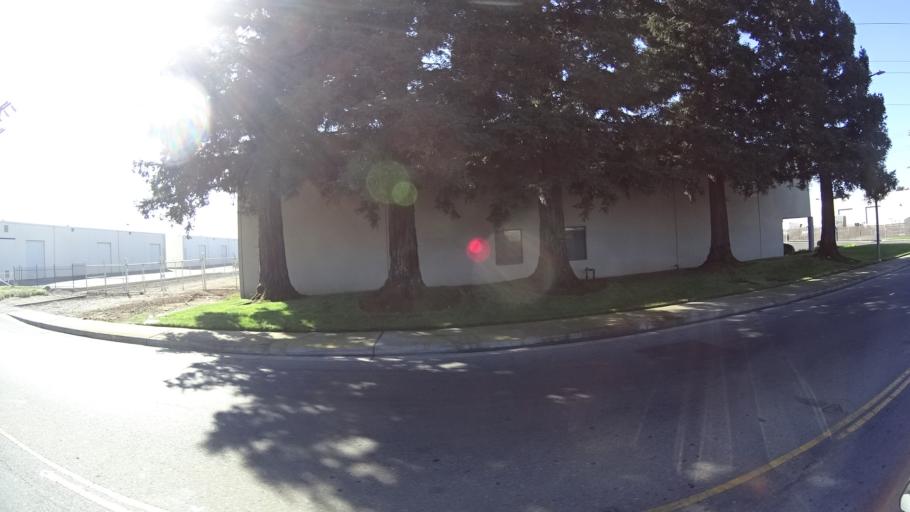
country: US
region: California
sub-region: Sacramento County
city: Rosemont
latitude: 38.5380
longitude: -121.4000
